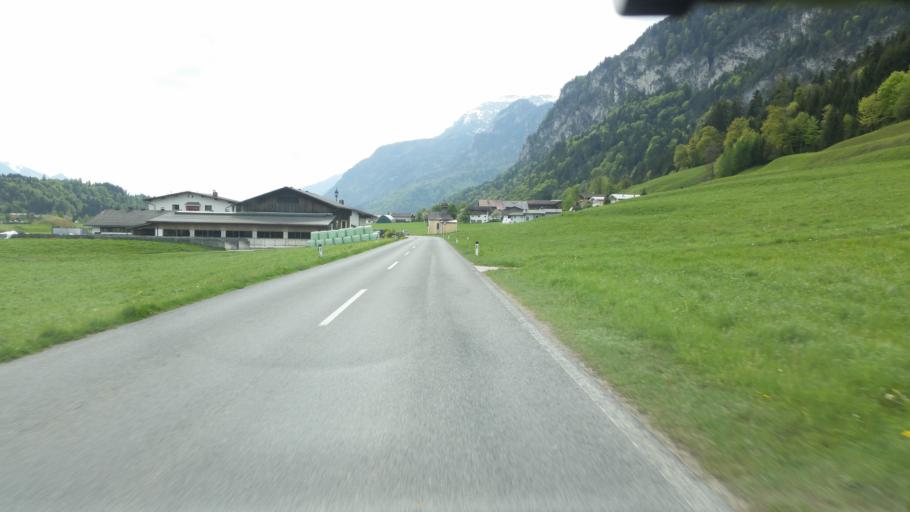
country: AT
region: Tyrol
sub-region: Politischer Bezirk Kufstein
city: Radfeld
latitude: 47.4683
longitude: 11.9150
